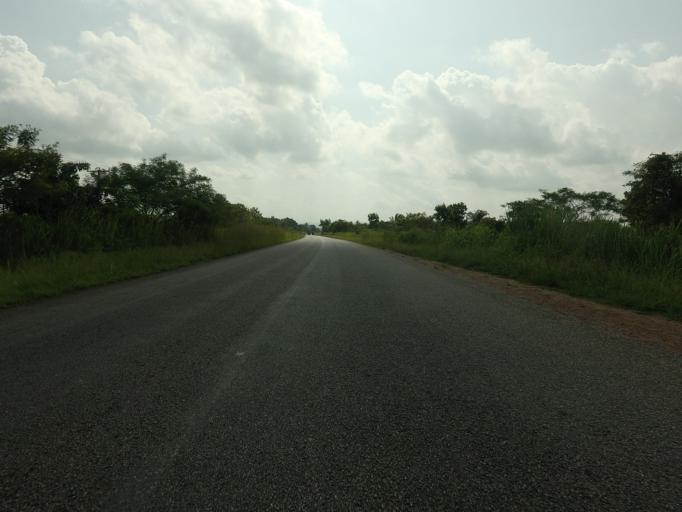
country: GH
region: Volta
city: Ho
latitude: 6.5855
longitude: 0.5720
